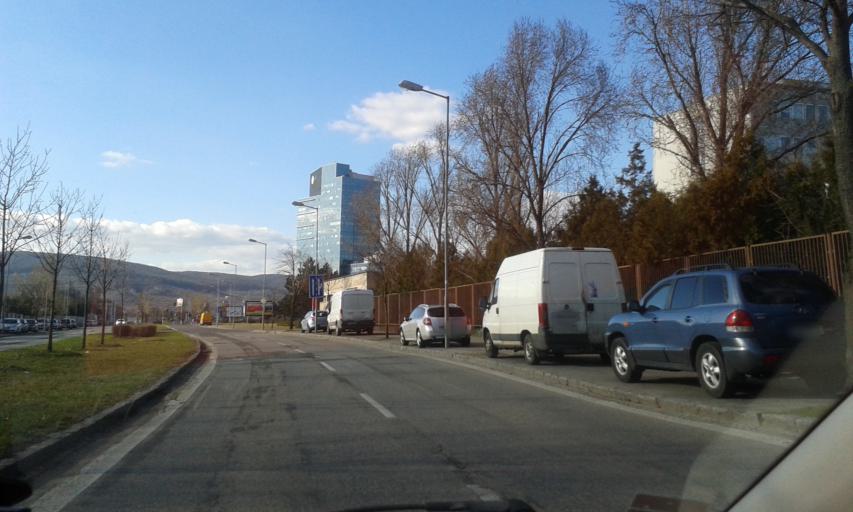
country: SK
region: Bratislavsky
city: Bratislava
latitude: 48.1696
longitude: 17.1479
